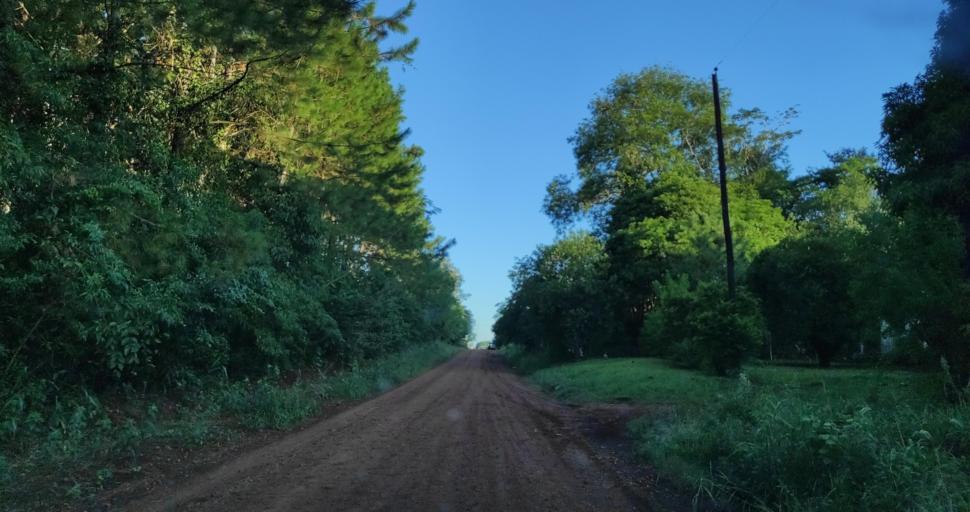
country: AR
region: Misiones
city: Gobernador Roca
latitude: -27.2232
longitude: -55.4330
